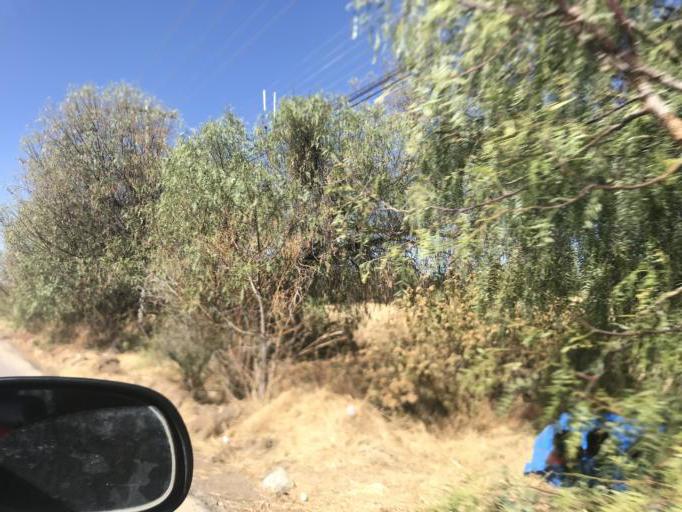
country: BO
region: Cochabamba
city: Tarata
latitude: -17.6111
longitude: -66.0159
